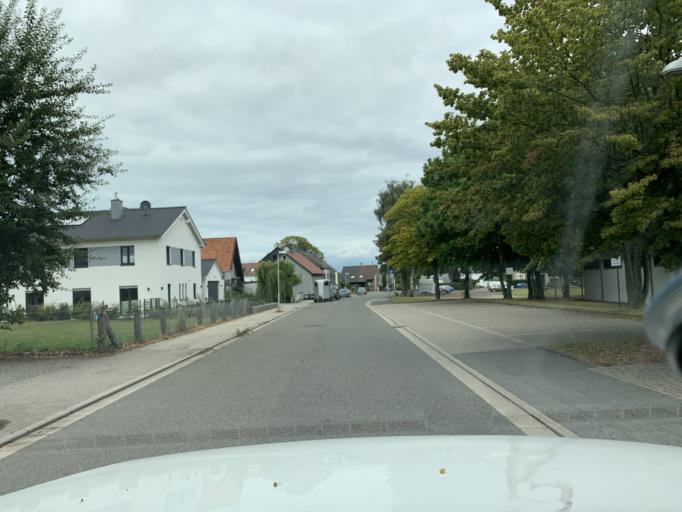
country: DE
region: North Rhine-Westphalia
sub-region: Regierungsbezirk Dusseldorf
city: Oberhausen
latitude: 51.4616
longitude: 6.9097
